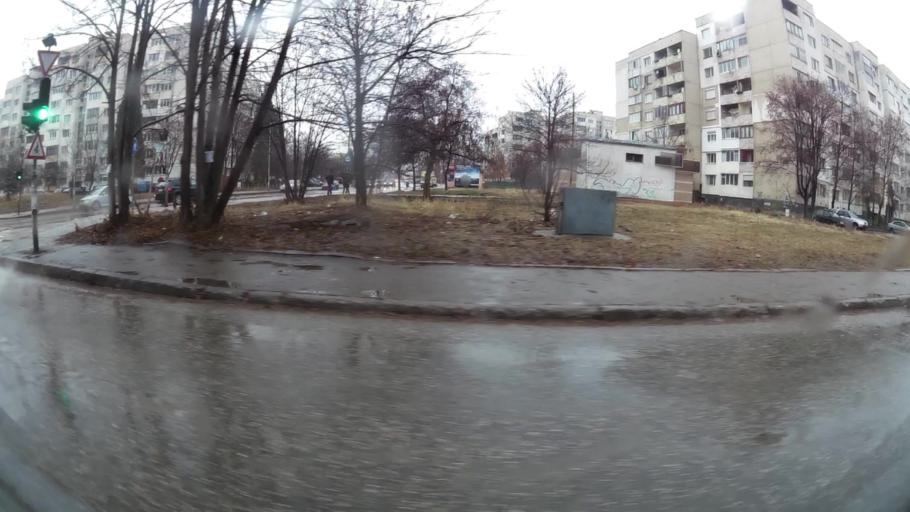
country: BG
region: Sofia-Capital
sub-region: Stolichna Obshtina
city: Sofia
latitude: 42.6374
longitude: 23.3804
